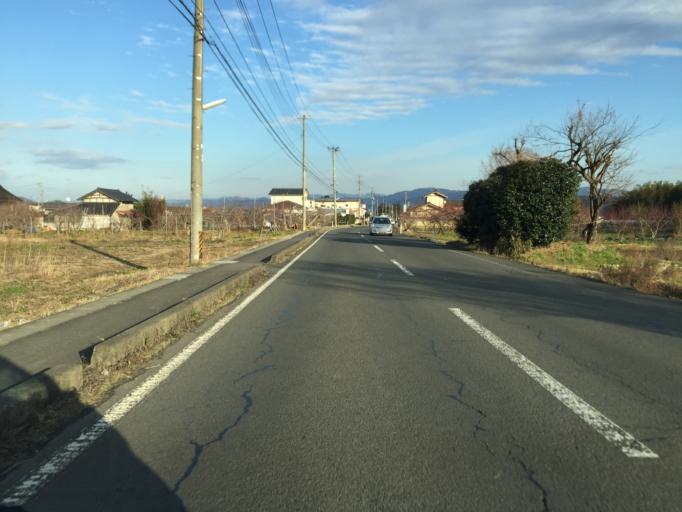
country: JP
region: Fukushima
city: Fukushima-shi
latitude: 37.7283
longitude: 140.4120
